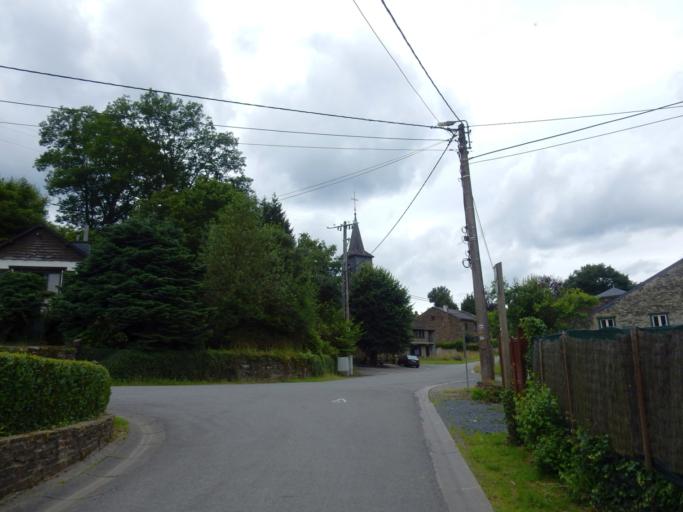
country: BE
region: Wallonia
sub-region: Province de Namur
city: Bievre
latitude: 49.8535
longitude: 4.9667
